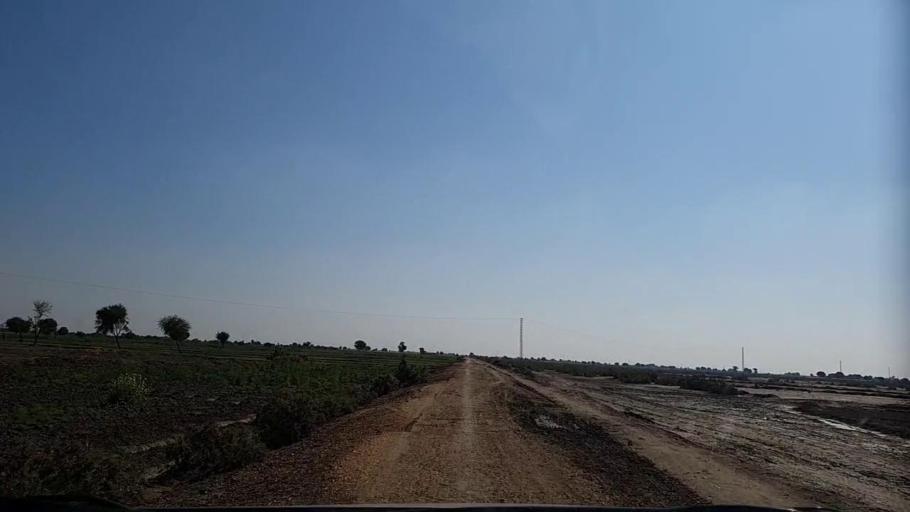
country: PK
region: Sindh
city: Pithoro
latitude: 25.7009
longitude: 69.3403
